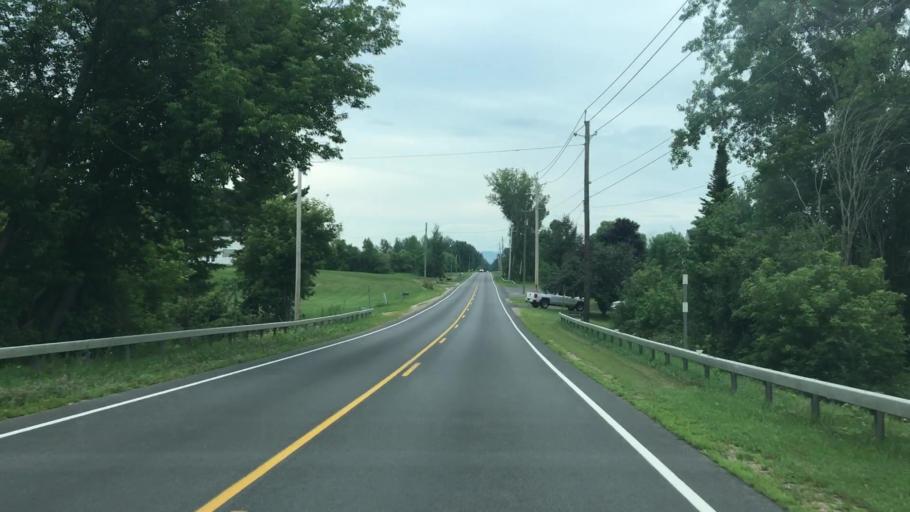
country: US
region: New York
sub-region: Clinton County
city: Peru
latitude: 44.5923
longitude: -73.5724
